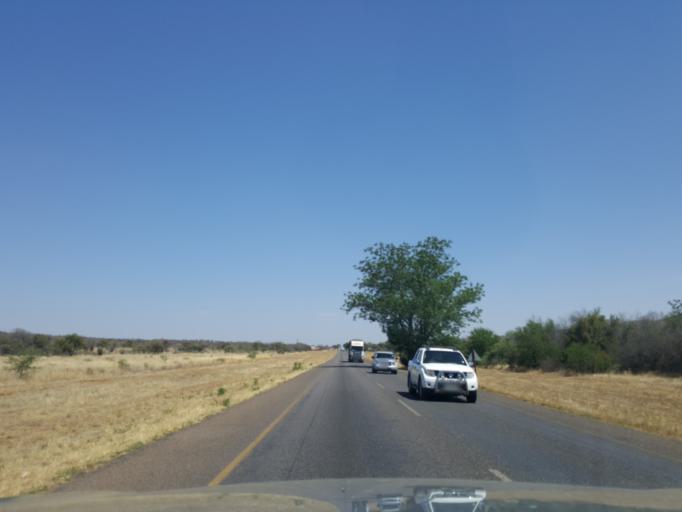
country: BW
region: South East
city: Lobatse
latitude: -25.1622
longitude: 25.6885
